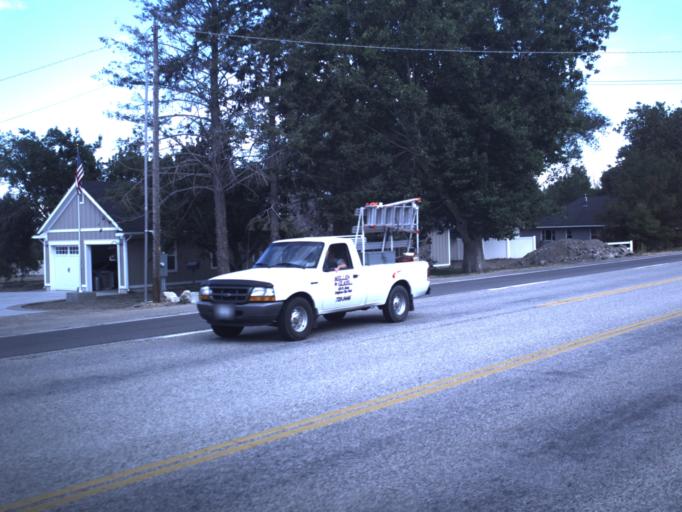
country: US
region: Utah
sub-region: Box Elder County
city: Willard
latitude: 41.4115
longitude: -112.0362
